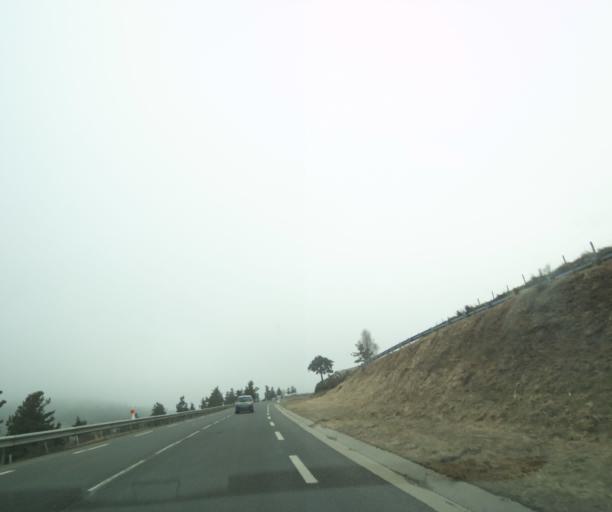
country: FR
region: Languedoc-Roussillon
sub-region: Departement de la Lozere
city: Langogne
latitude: 44.6737
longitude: 3.7649
